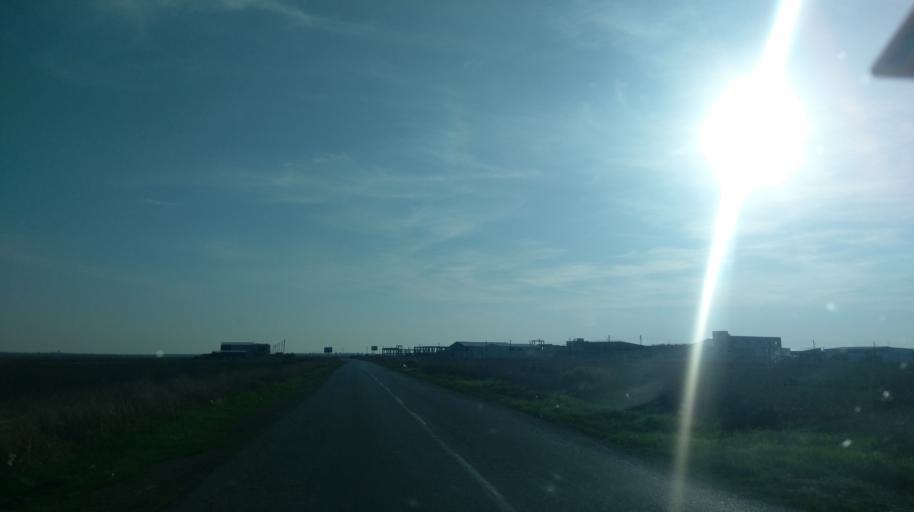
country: CY
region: Ammochostos
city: Acheritou
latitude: 35.1369
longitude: 33.8728
